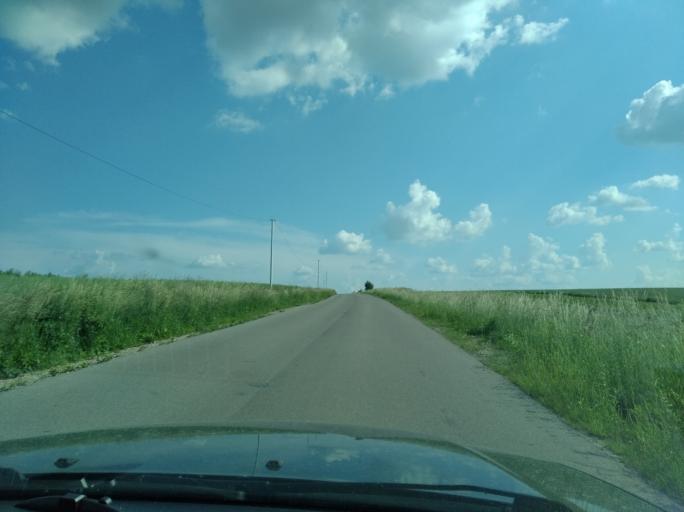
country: PL
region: Subcarpathian Voivodeship
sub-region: Powiat jaroslawski
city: Ostrow
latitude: 49.9347
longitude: 22.7399
